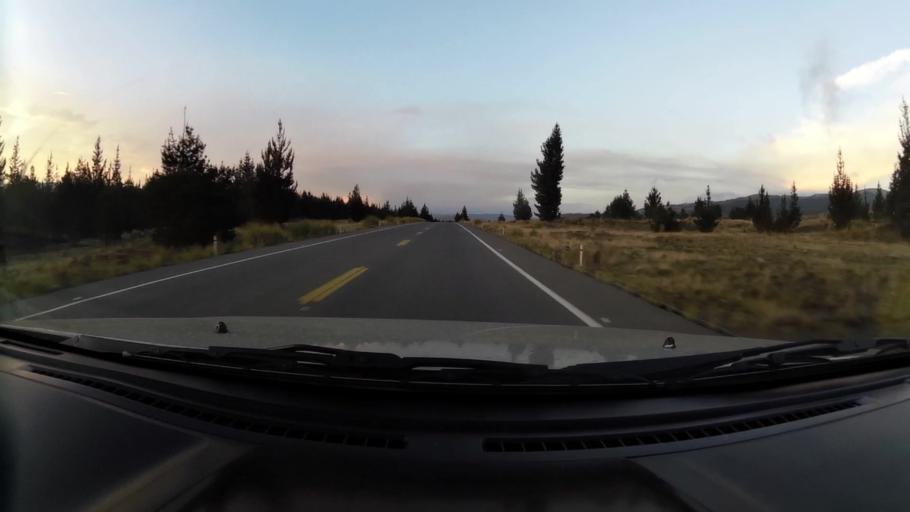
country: EC
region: Chimborazo
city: Alausi
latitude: -2.0307
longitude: -78.7352
